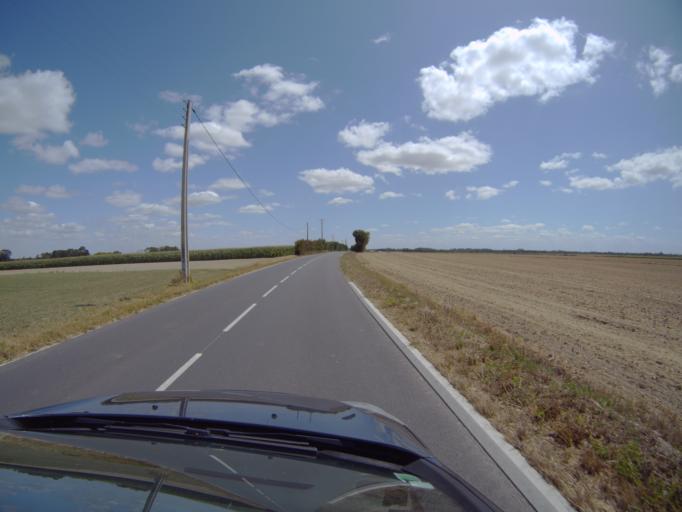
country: FR
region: Poitou-Charentes
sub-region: Departement de la Charente-Maritime
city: Saint-Jean-de-Liversay
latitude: 46.2833
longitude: -0.9232
